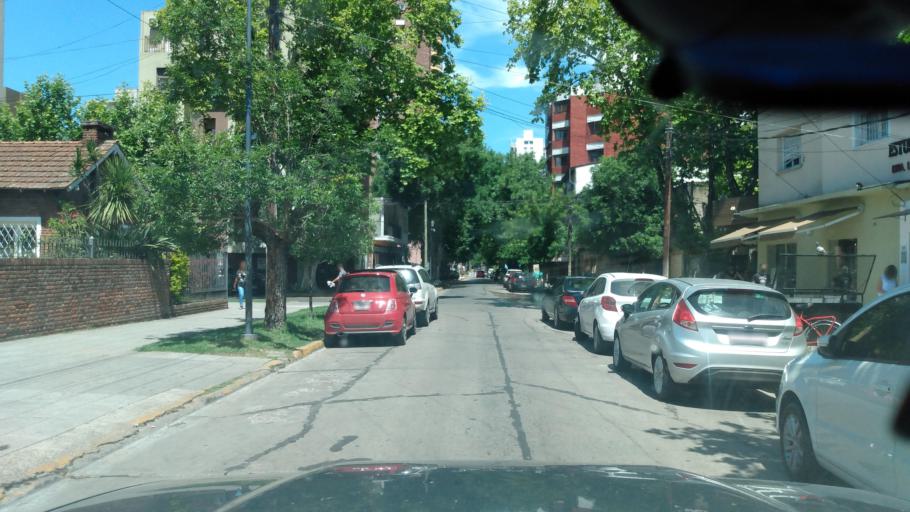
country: AR
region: Buenos Aires
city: Hurlingham
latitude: -34.5430
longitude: -58.7075
